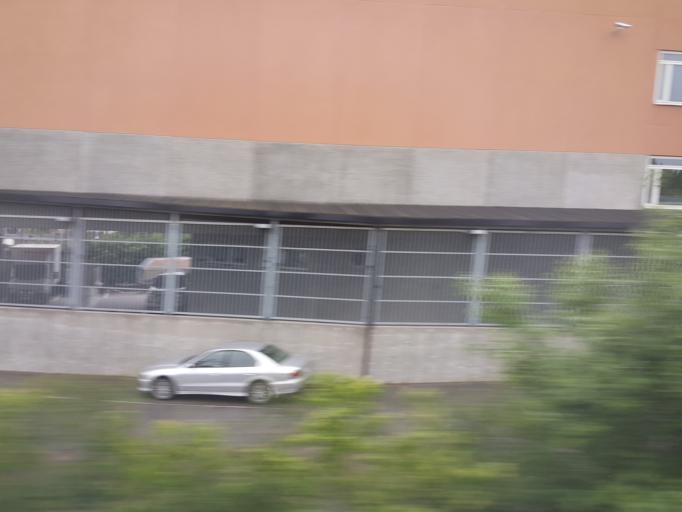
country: SE
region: Uppsala
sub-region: Uppsala Kommun
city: Uppsala
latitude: 59.8655
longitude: 17.6328
